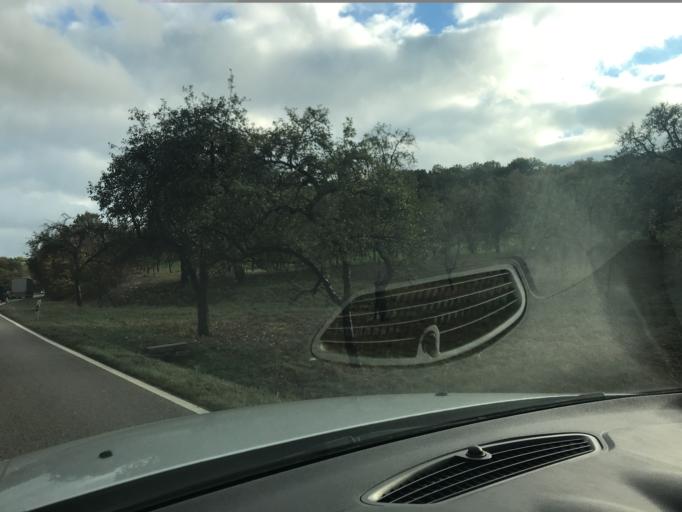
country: DE
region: Baden-Wuerttemberg
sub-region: Regierungsbezirk Stuttgart
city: Grossbottwar
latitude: 48.9916
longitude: 9.3042
